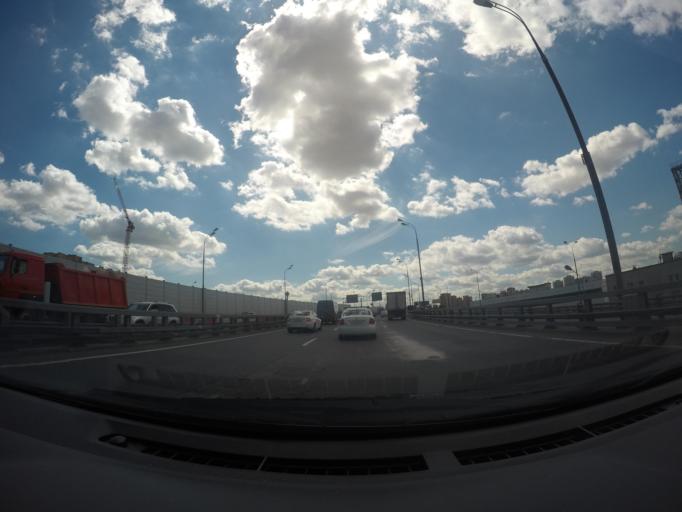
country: RU
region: Moscow
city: Lefortovo
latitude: 55.7468
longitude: 37.6998
